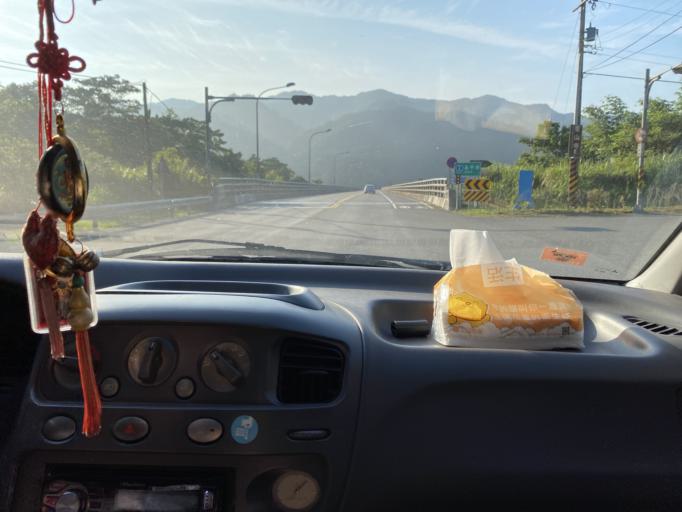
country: TW
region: Taiwan
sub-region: Keelung
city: Keelung
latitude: 25.0485
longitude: 121.7774
